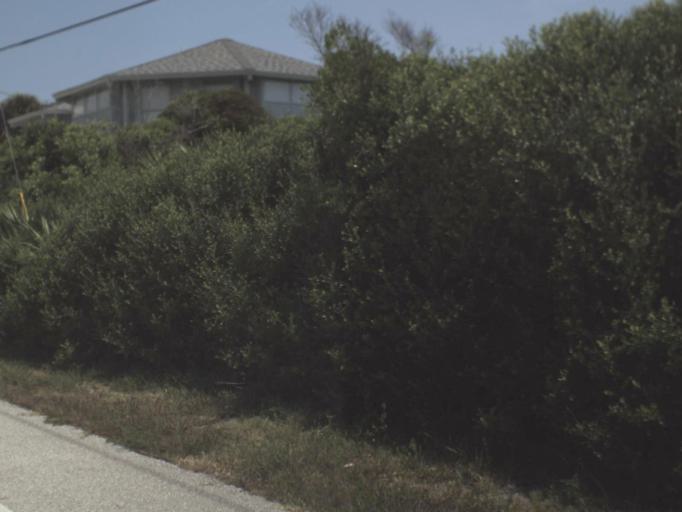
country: US
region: Florida
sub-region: Saint Johns County
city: Villano Beach
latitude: 29.9785
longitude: -81.3122
